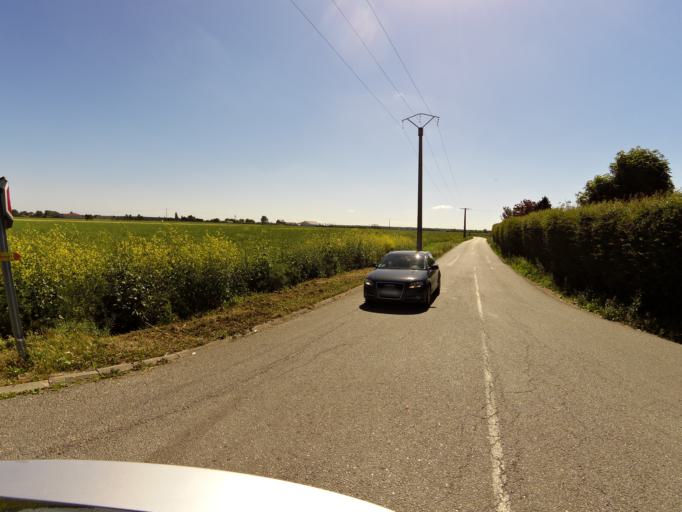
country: FR
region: Nord-Pas-de-Calais
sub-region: Departement du Nord
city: Teteghem
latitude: 51.0021
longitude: 2.4549
